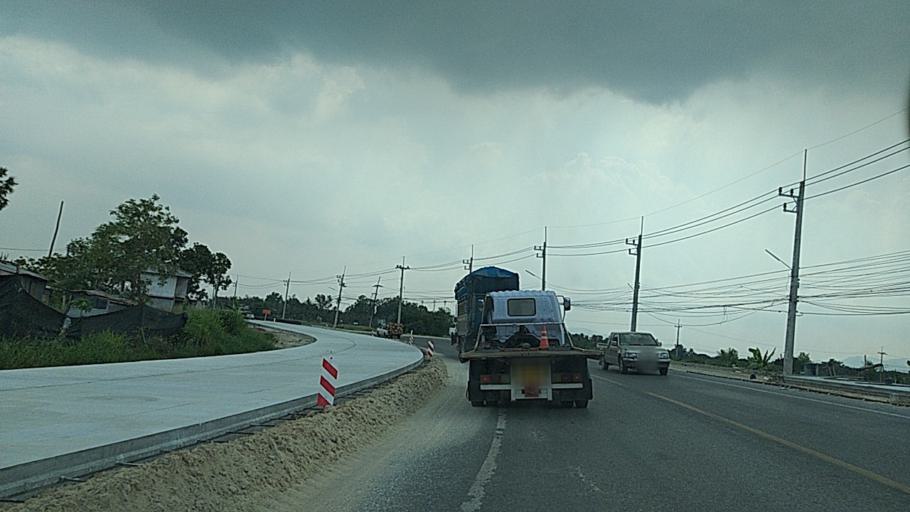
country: TH
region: Chon Buri
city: Ban Bueng
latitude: 13.3166
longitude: 101.1838
